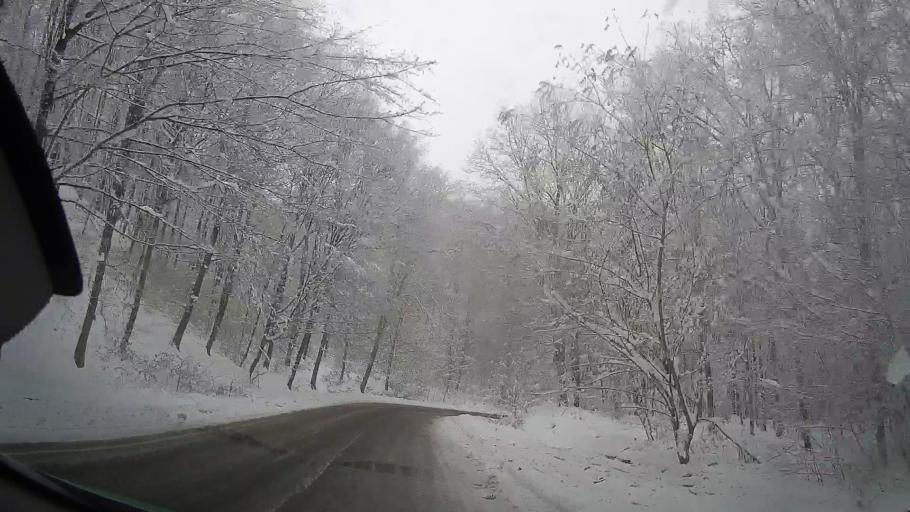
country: RO
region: Neamt
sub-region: Comuna Valea Ursului
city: Valea Ursului
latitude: 46.8481
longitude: 27.0653
